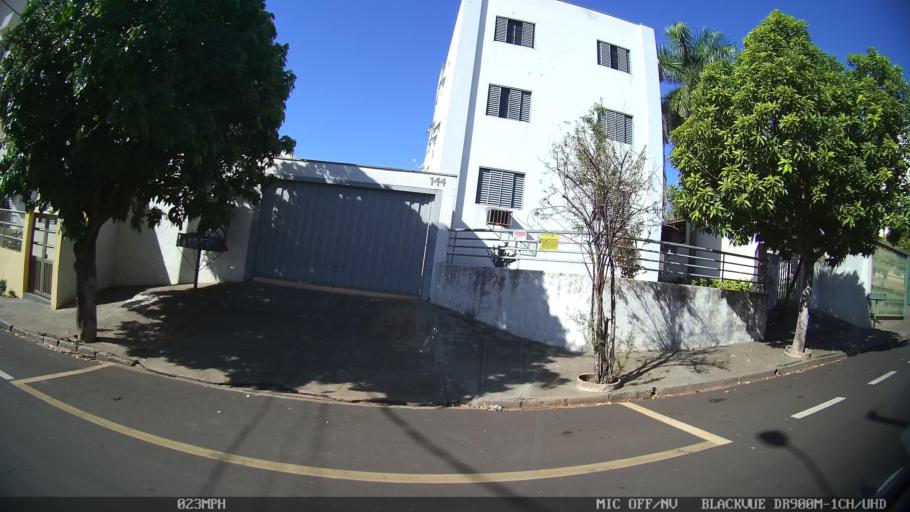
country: BR
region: Sao Paulo
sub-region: Olimpia
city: Olimpia
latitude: -20.7347
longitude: -48.9184
